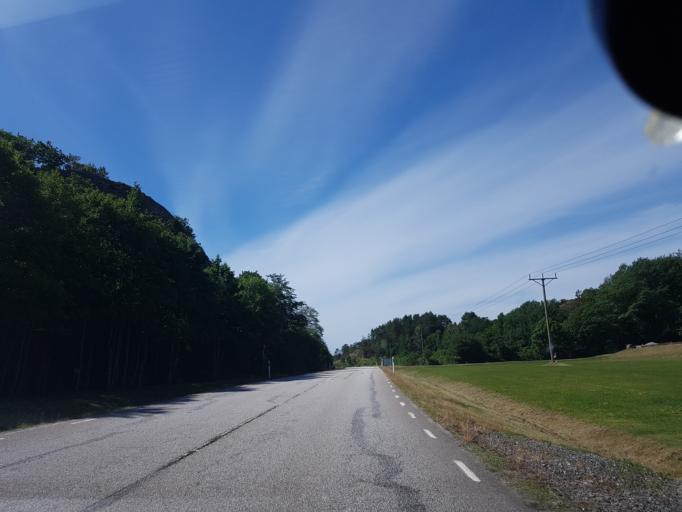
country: SE
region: Vaestra Goetaland
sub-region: Lysekils Kommun
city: Lysekil
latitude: 58.1623
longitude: 11.4766
